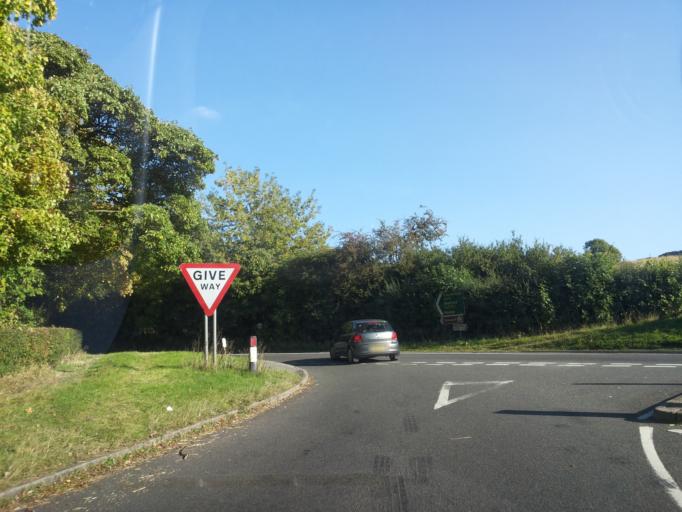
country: GB
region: England
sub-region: Derbyshire
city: Bakewell
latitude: 53.2295
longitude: -1.6617
